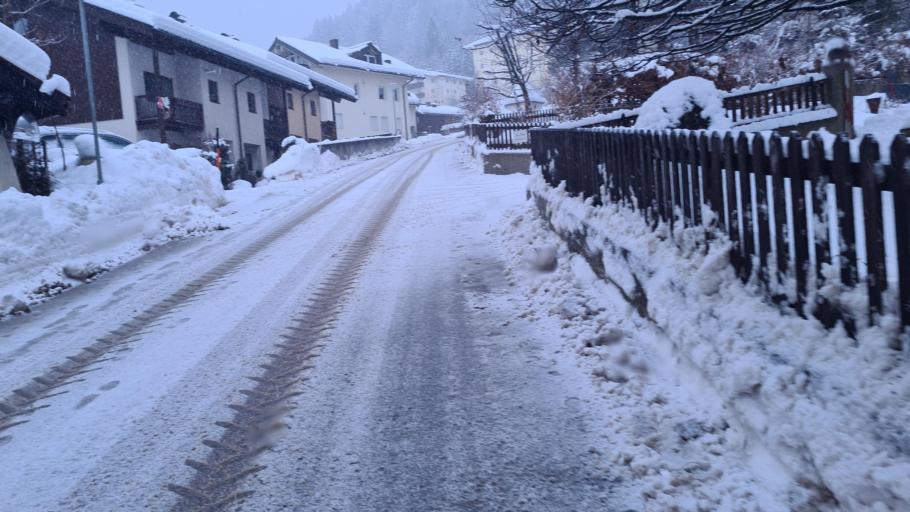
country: AT
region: Salzburg
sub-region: Politischer Bezirk Zell am See
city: Neukirchen am Grossvenediger
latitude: 47.2549
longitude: 12.2757
